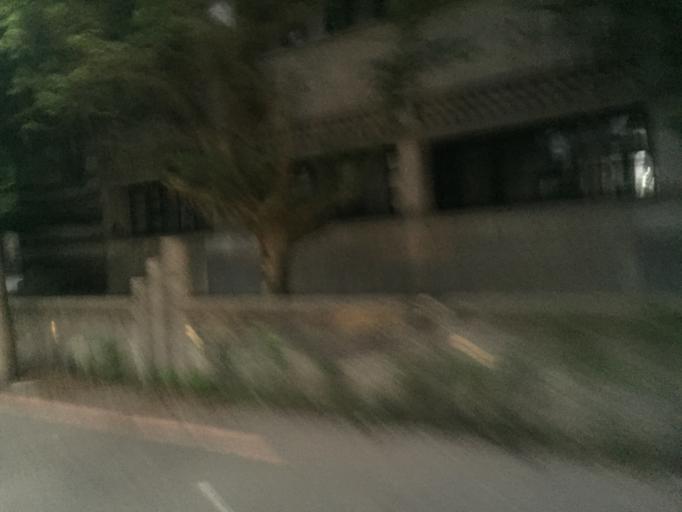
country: TW
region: Taiwan
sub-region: Yilan
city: Yilan
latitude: 24.7547
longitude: 121.7461
